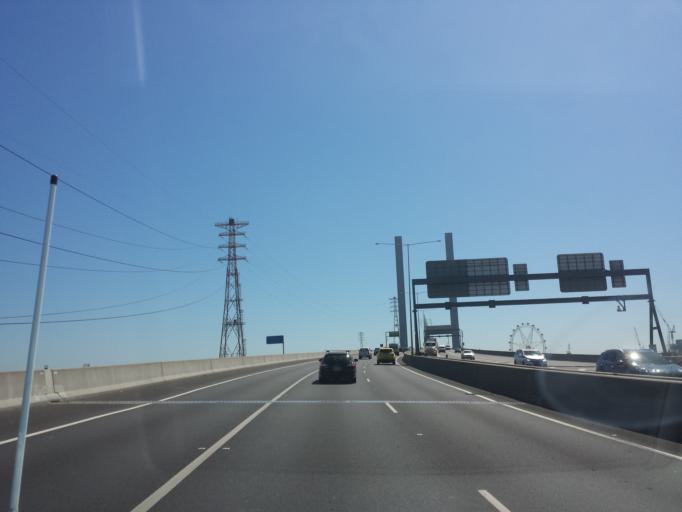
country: AU
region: Victoria
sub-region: Port Phillip
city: Port Melbourne
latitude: -37.8242
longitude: 144.9306
